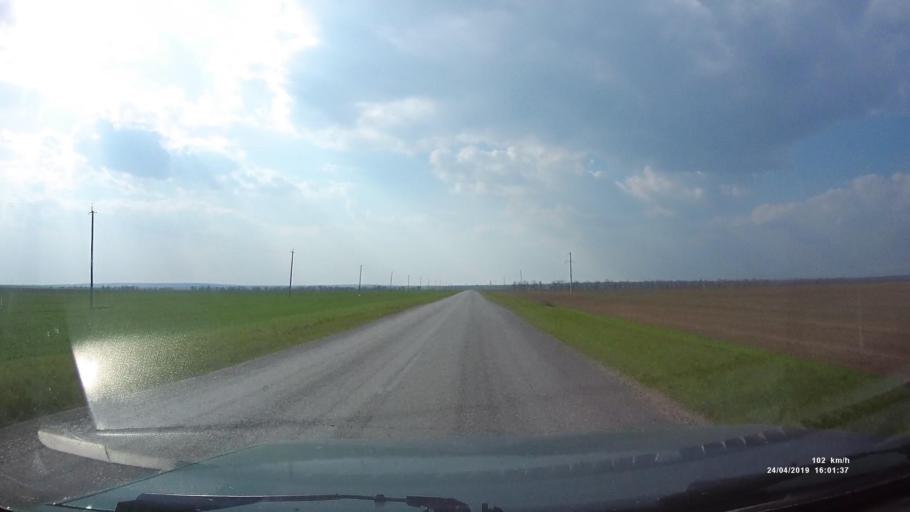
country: RU
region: Rostov
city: Sovetskoye
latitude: 46.6434
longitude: 42.4328
